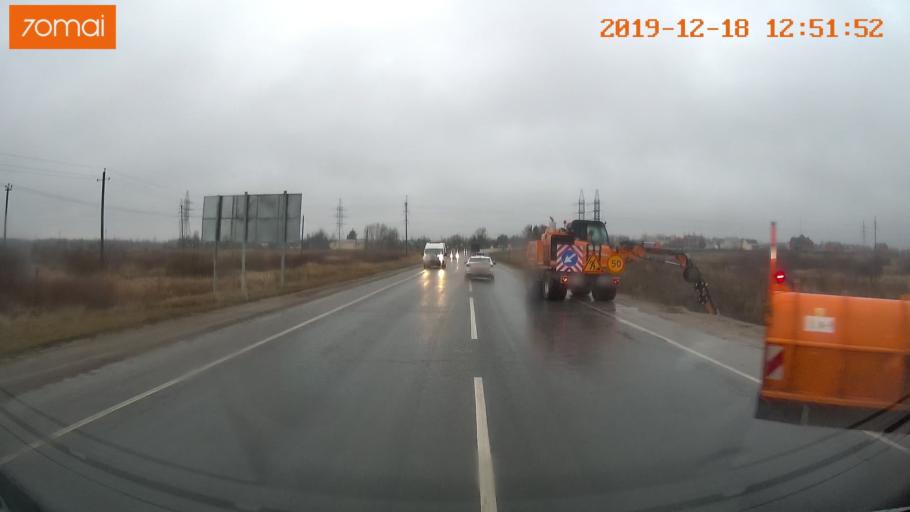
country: RU
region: Moskovskaya
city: Klin
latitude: 56.3072
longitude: 36.6854
